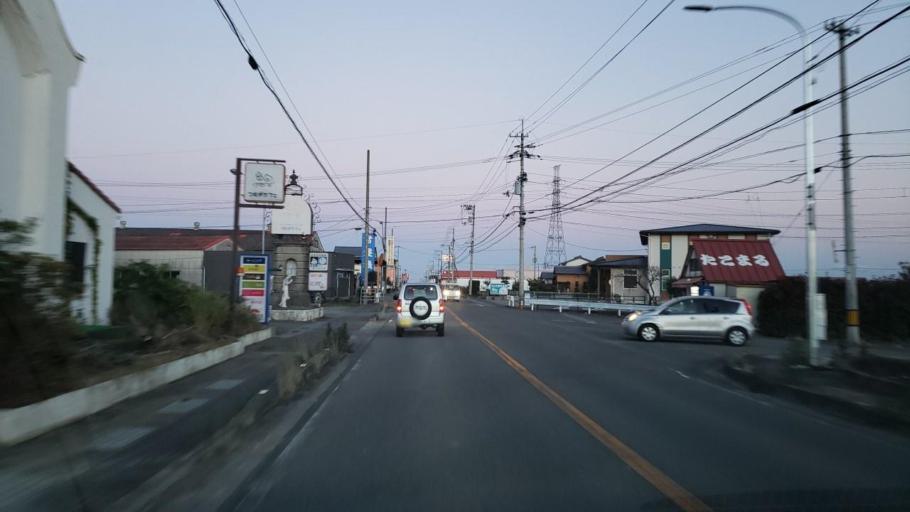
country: JP
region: Tokushima
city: Ishii
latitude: 34.1206
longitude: 134.4423
